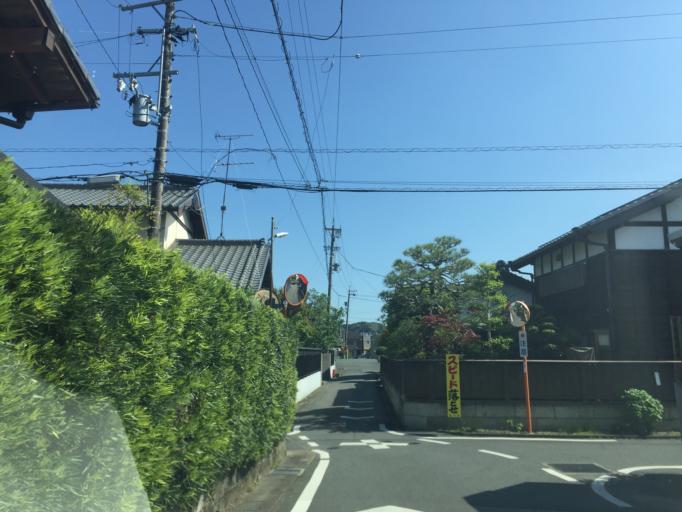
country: JP
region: Shizuoka
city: Kakegawa
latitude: 34.7742
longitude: 138.0221
